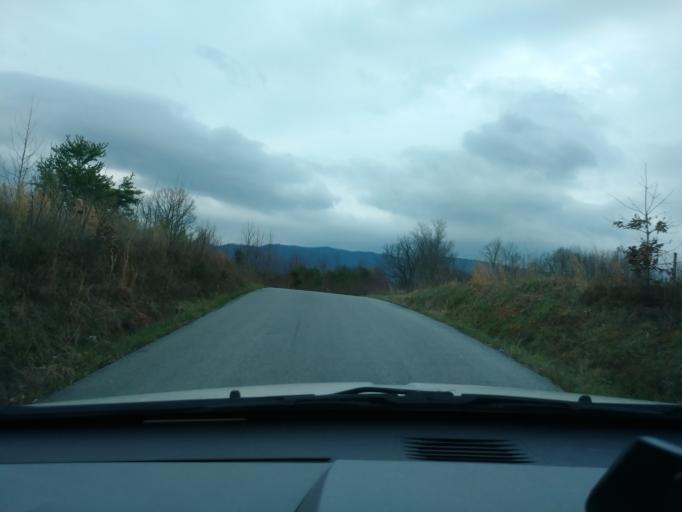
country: US
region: Tennessee
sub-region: Greene County
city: Tusculum
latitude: 36.0916
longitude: -82.7498
